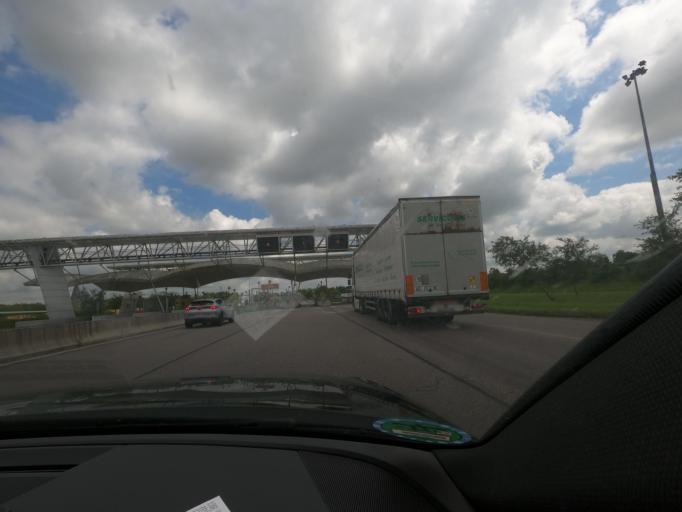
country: FR
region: Haute-Normandie
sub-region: Departement de la Seine-Maritime
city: Sainte-Marie-des-Champs
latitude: 49.6276
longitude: 0.8054
